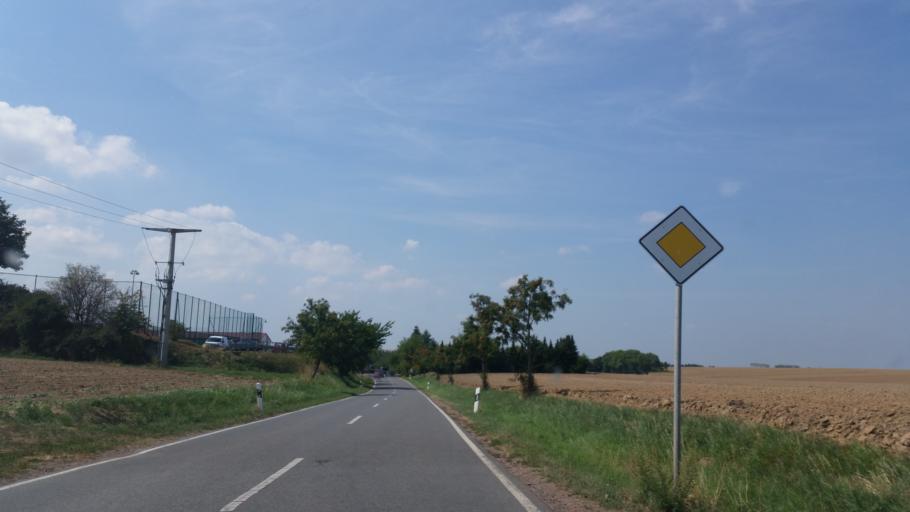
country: DE
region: Saxony
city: Wilsdruff
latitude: 51.0676
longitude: 13.5474
